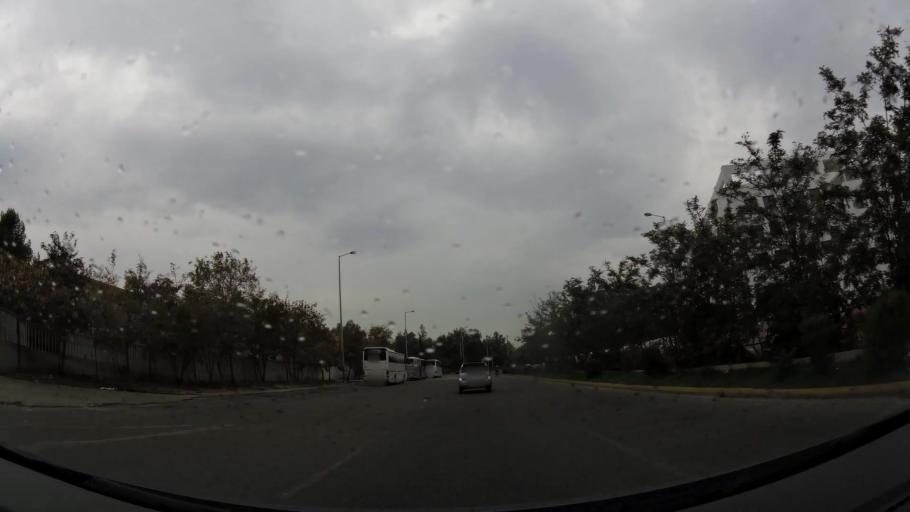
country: GR
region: Attica
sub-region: Nomarchia Athinas
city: Palaio Faliro
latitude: 37.9378
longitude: 23.6951
